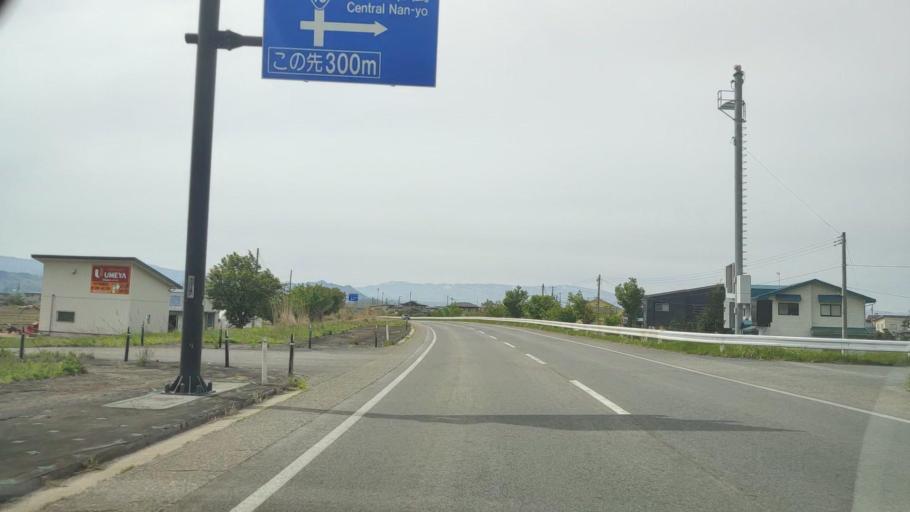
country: JP
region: Yamagata
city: Takahata
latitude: 38.0523
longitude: 140.1734
